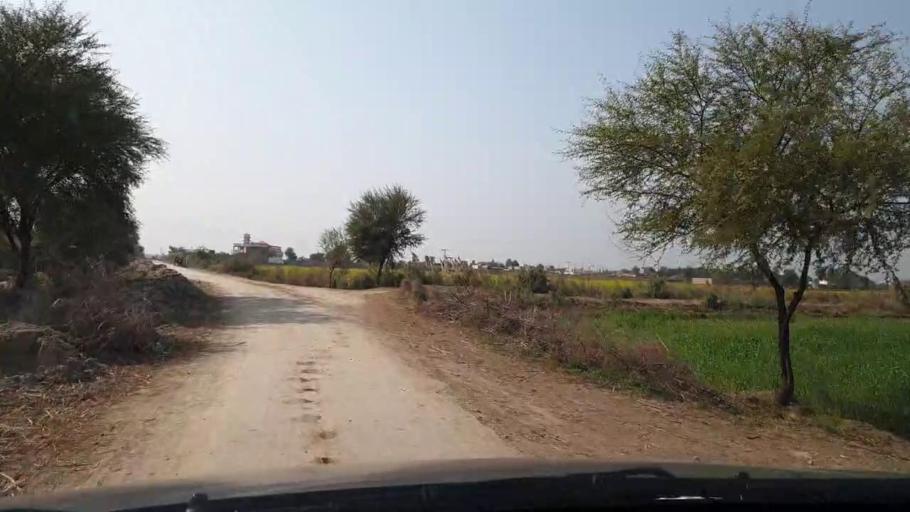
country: PK
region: Sindh
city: Jhol
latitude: 26.0030
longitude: 68.9096
